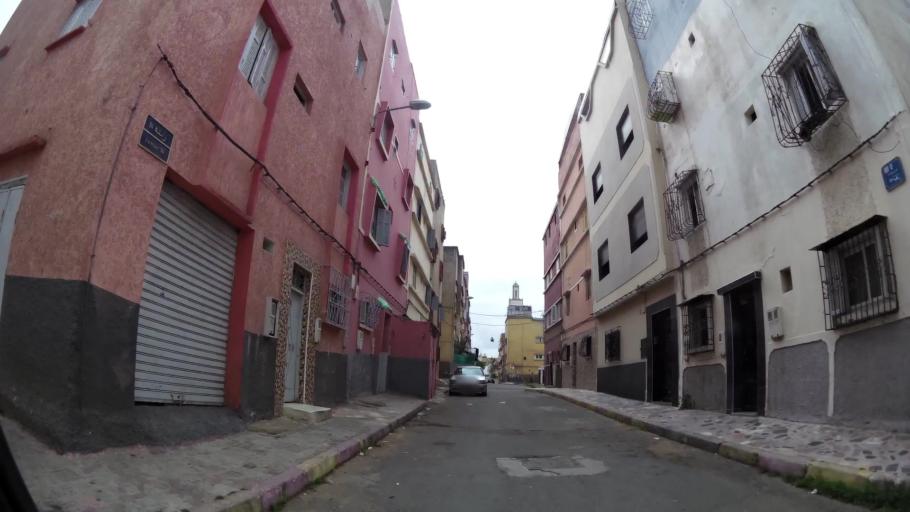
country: MA
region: Grand Casablanca
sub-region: Casablanca
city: Casablanca
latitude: 33.5660
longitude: -7.5579
